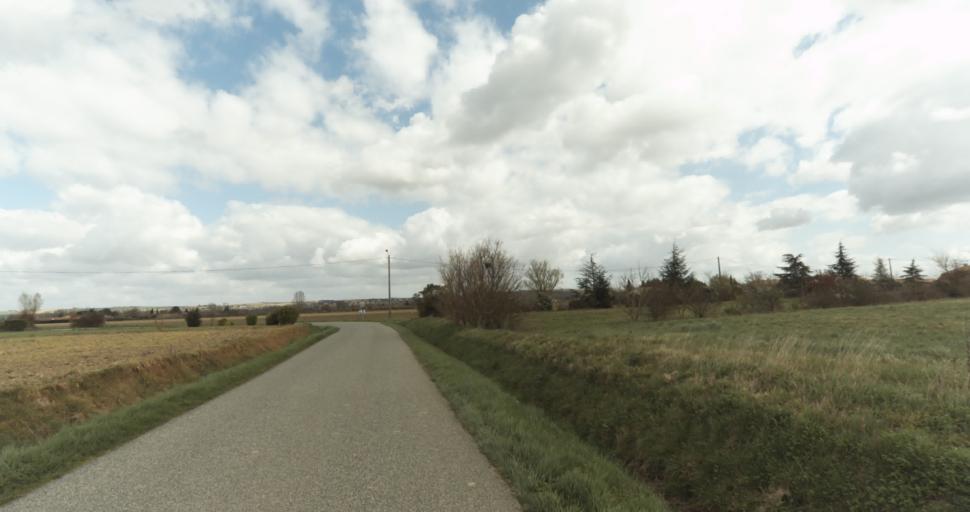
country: FR
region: Midi-Pyrenees
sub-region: Departement de la Haute-Garonne
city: Auterive
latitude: 43.3288
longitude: 1.4695
